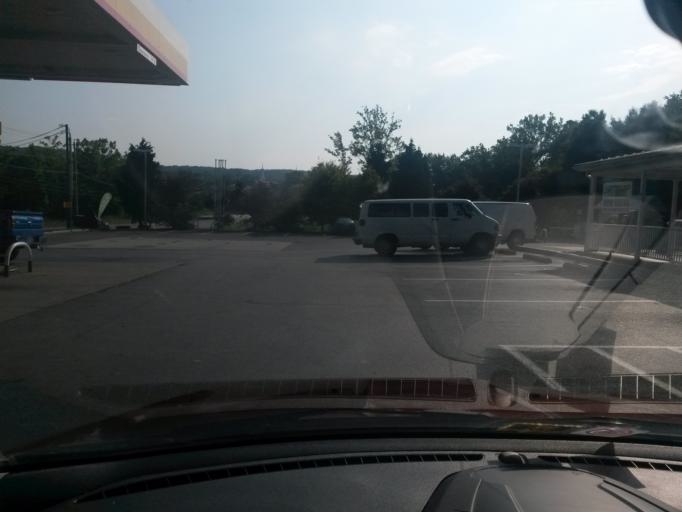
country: US
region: Virginia
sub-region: Giles County
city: Narrows
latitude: 37.3962
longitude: -80.8026
